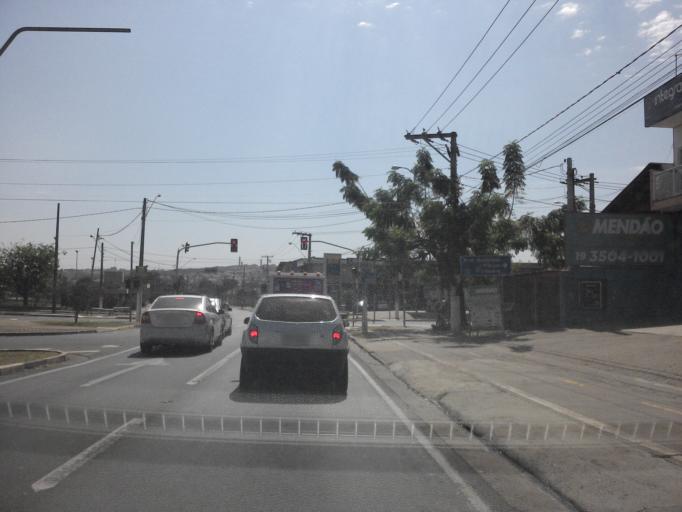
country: BR
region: Sao Paulo
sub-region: Hortolandia
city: Hortolandia
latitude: -22.8681
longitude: -47.2253
